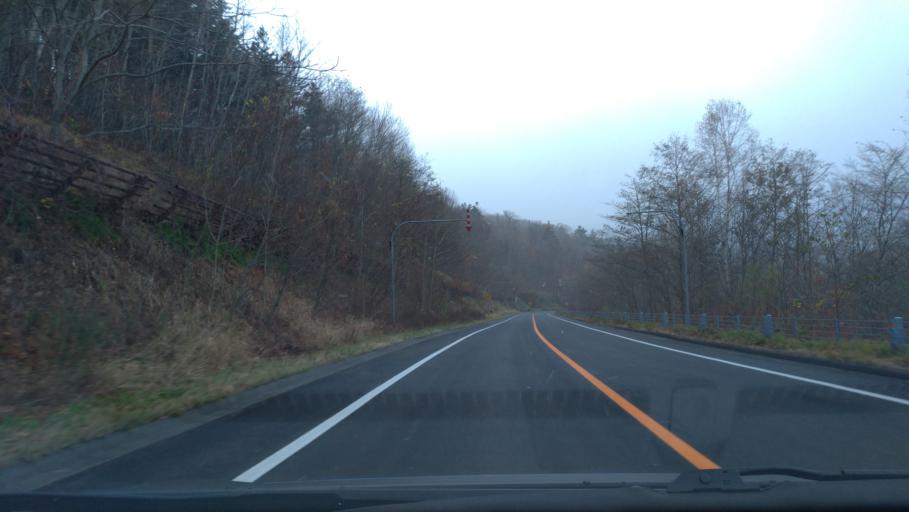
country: JP
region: Hokkaido
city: Shiraoi
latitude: 42.7435
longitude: 141.4105
